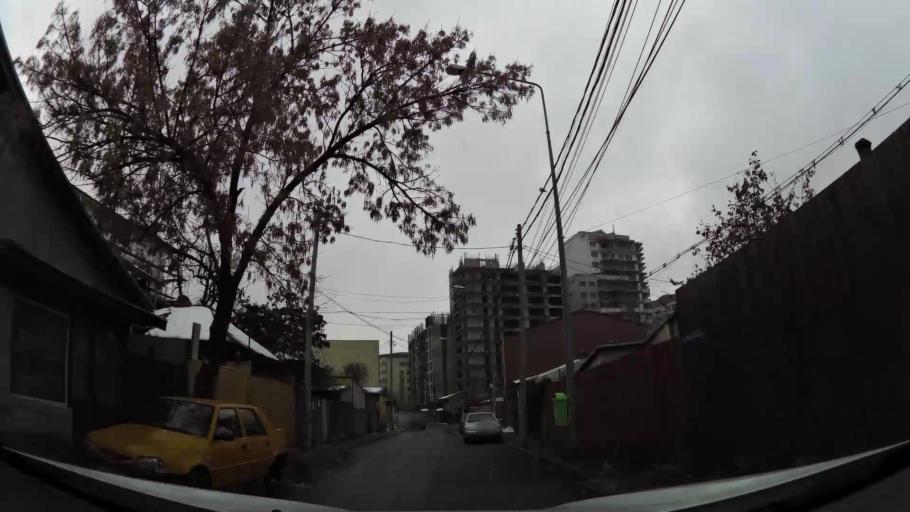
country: RO
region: Bucuresti
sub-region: Municipiul Bucuresti
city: Bucharest
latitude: 44.4142
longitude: 26.1258
